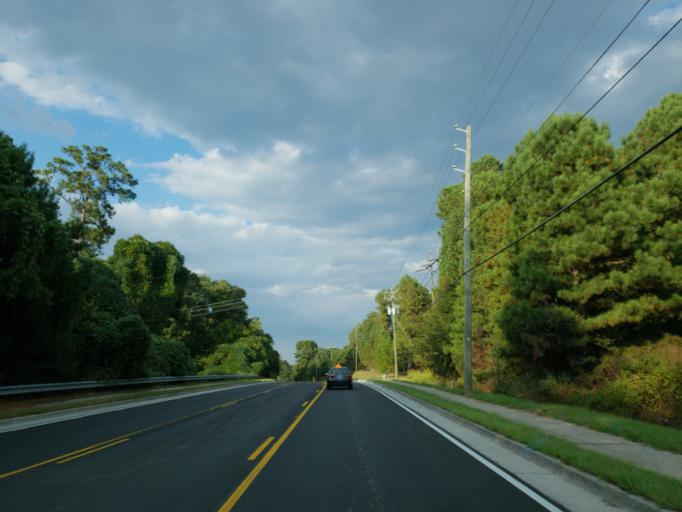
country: US
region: Georgia
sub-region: Cobb County
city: Vinings
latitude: 33.8139
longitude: -84.5025
